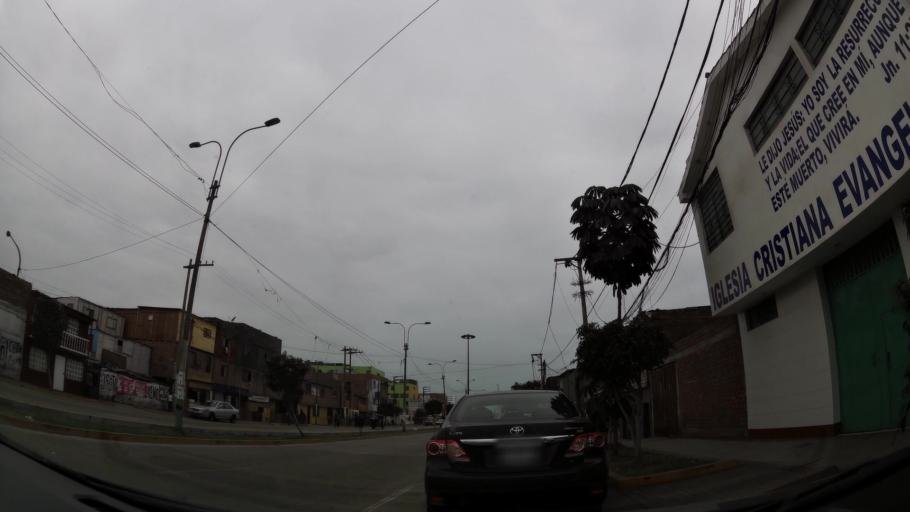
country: PE
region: Callao
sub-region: Callao
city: Callao
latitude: -12.0488
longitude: -77.1348
